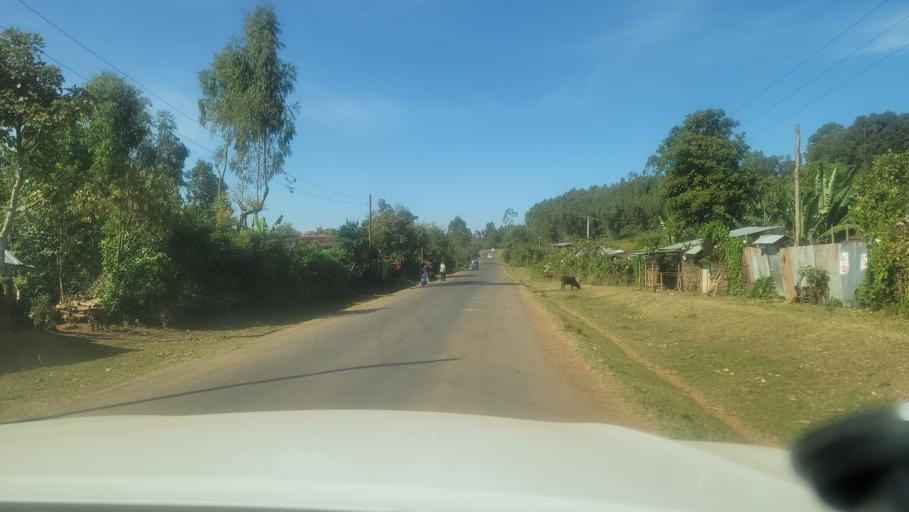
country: ET
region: Oromiya
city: Agaro
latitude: 7.7966
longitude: 36.4857
